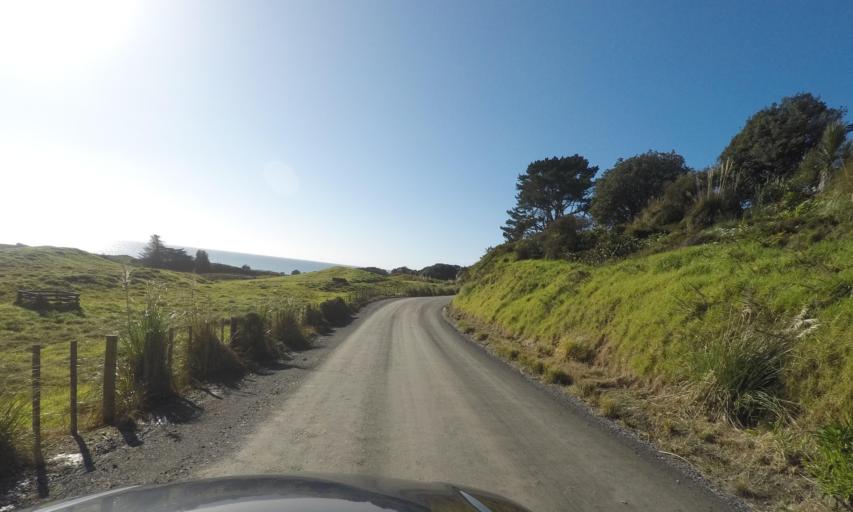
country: NZ
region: Auckland
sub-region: Auckland
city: Wellsford
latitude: -36.1606
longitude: 174.6436
